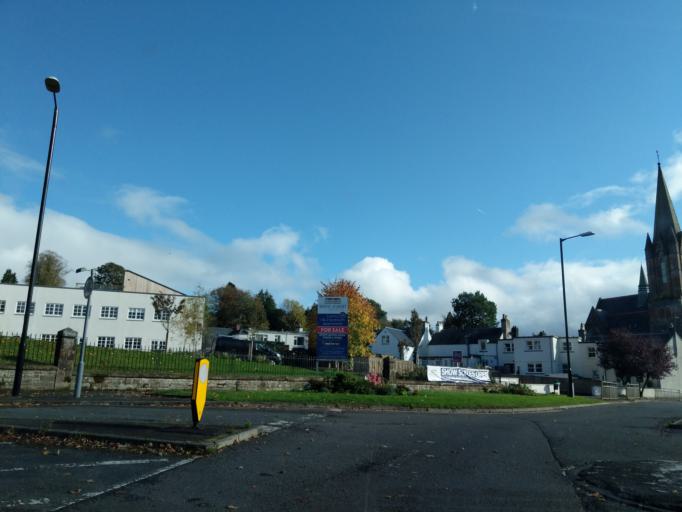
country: GB
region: Scotland
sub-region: Dumfries and Galloway
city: Moffat
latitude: 55.3361
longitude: -3.4463
